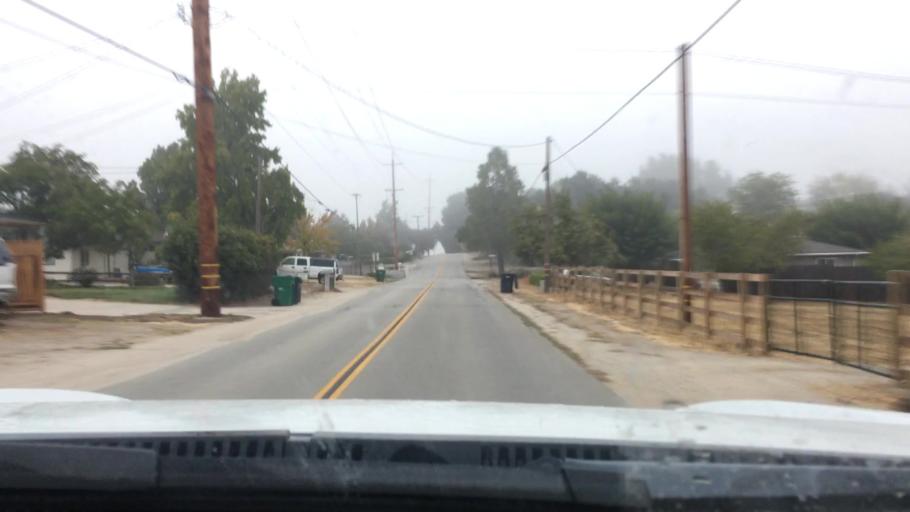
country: US
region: California
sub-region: San Luis Obispo County
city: Atascadero
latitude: 35.4876
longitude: -120.6860
